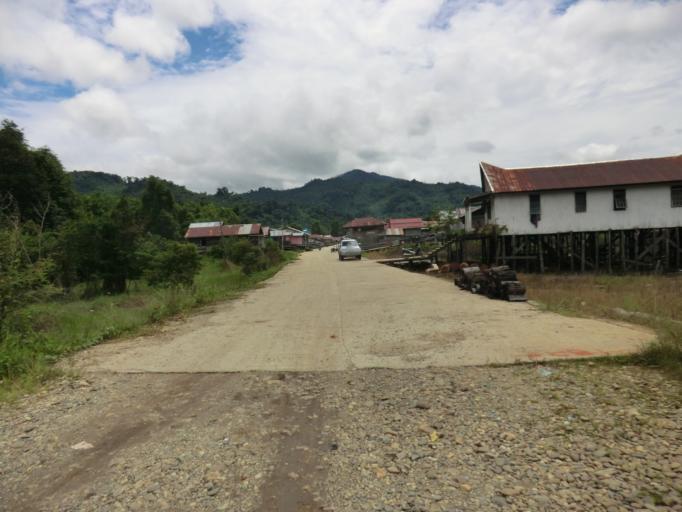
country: MY
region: Sarawak
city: Simanggang
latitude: 1.0299
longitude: 112.2256
